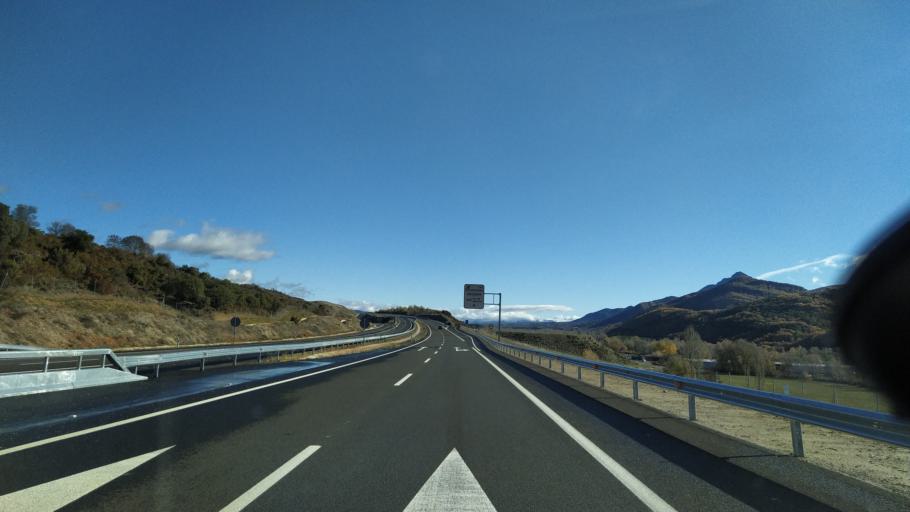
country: ES
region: Aragon
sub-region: Provincia de Huesca
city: Santa Cruz de la Seros
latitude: 42.5613
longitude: -0.6633
